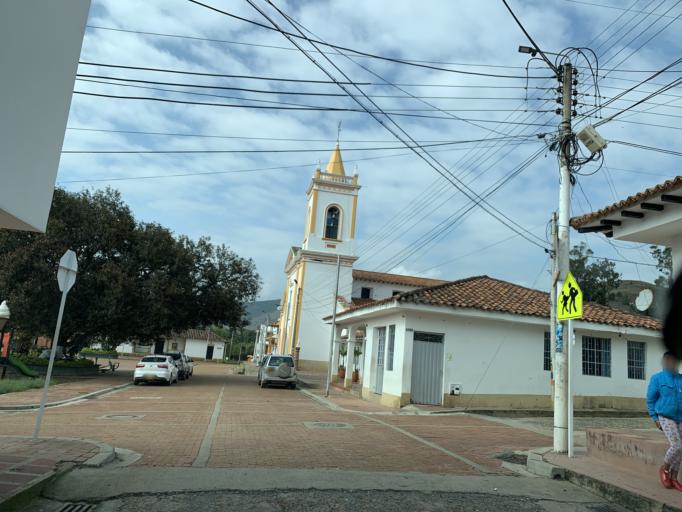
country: CO
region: Boyaca
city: Raquira
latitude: 5.5800
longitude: -73.6470
